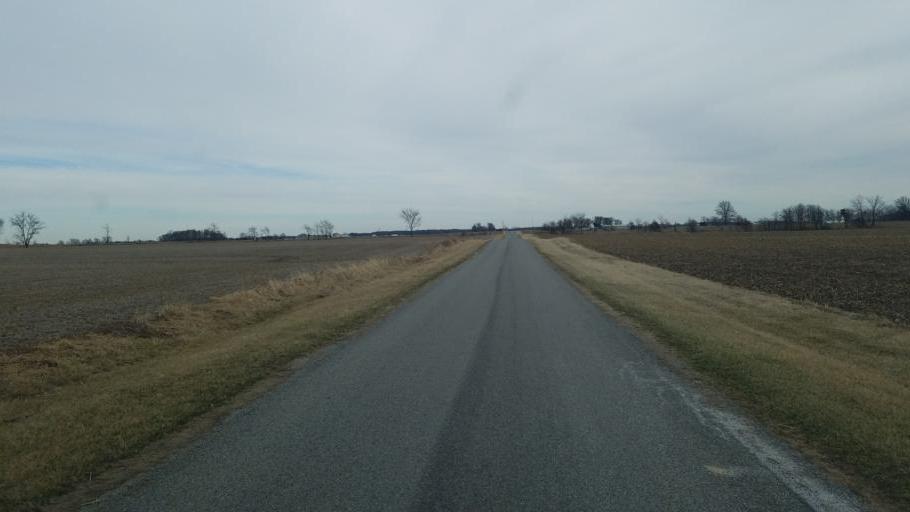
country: US
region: Ohio
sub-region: Union County
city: Richwood
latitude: 40.4953
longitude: -83.3636
